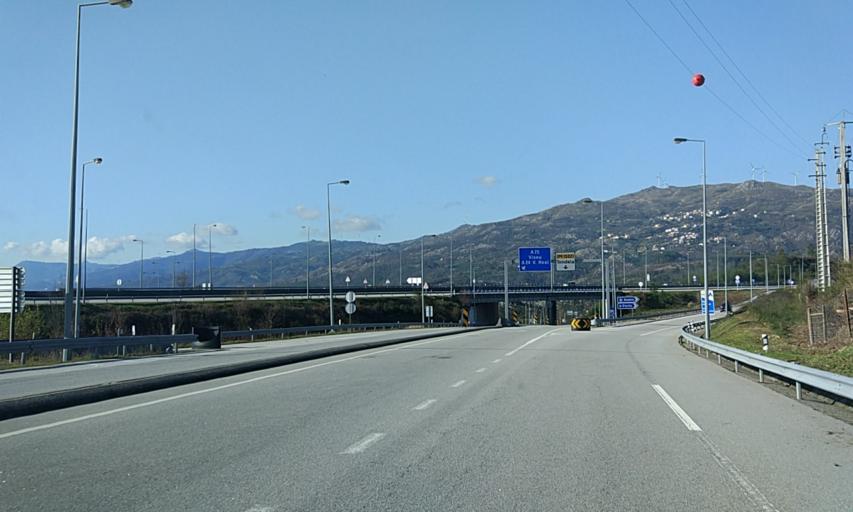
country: PT
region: Viseu
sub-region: Vouzela
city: Vouzela
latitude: 40.6487
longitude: -8.0591
